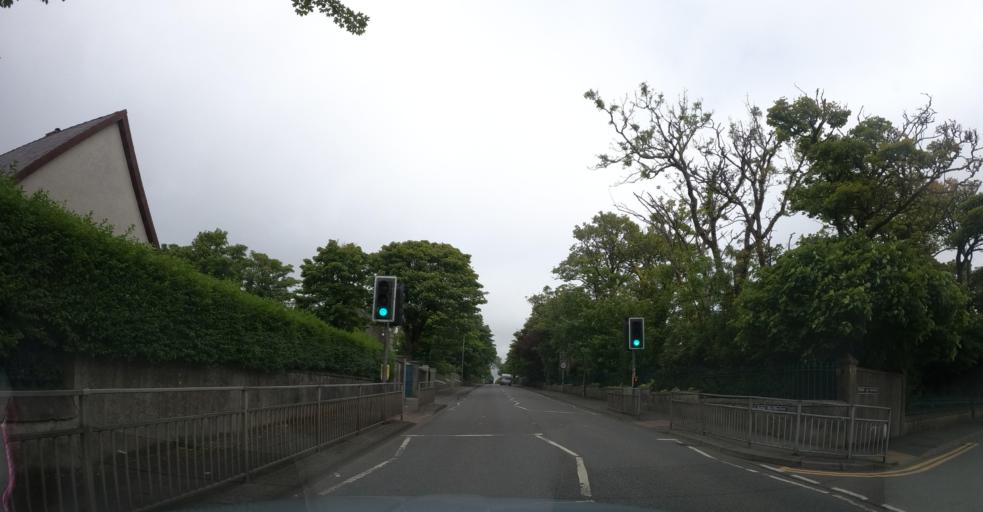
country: GB
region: Scotland
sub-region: Eilean Siar
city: Stornoway
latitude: 58.2095
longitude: -6.3819
